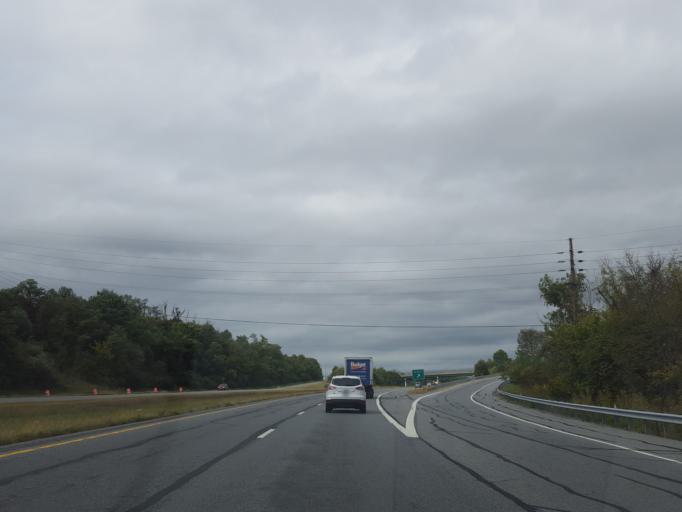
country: US
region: Maryland
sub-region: Frederick County
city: Jefferson
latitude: 39.3548
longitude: -77.5777
